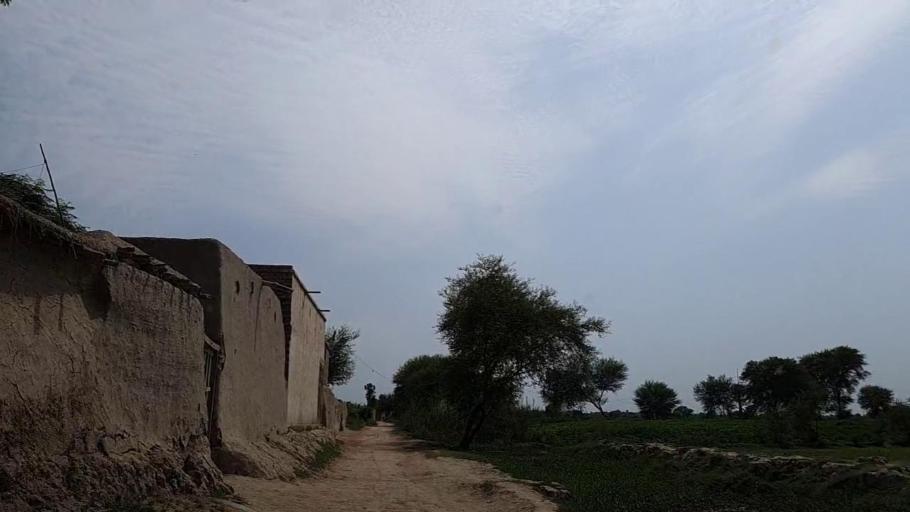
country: PK
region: Sindh
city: Khanpur
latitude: 27.8571
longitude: 69.4261
